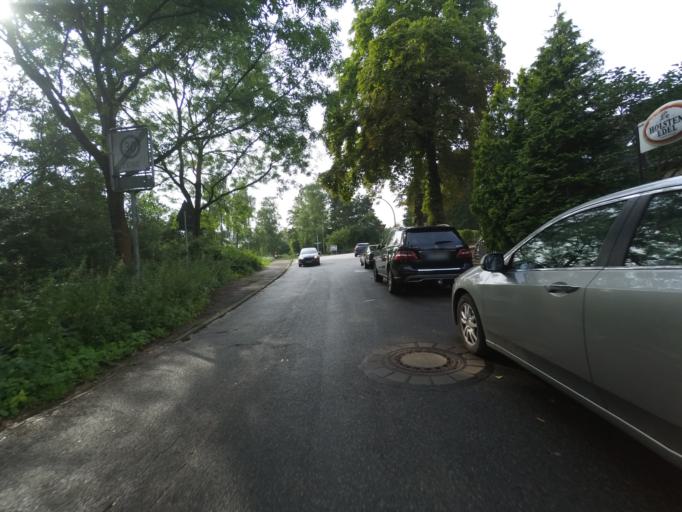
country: DE
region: Hamburg
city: Bergedorf
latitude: 53.4981
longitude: 10.1833
